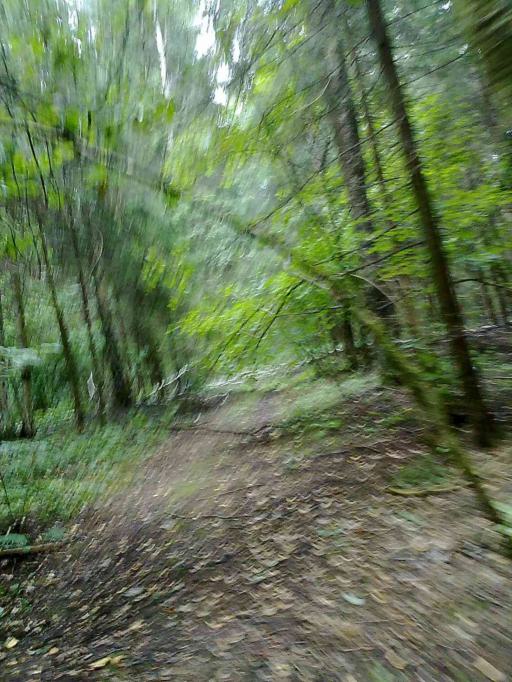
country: RU
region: Moskovskaya
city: Filimonki
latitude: 55.5530
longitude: 37.3788
